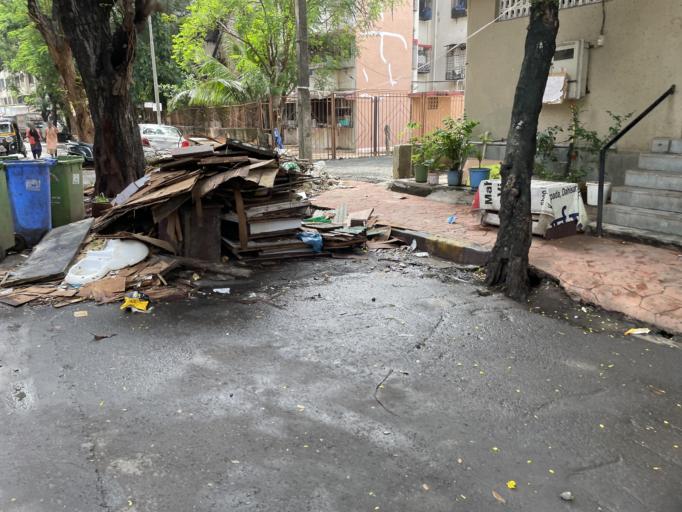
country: IN
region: Maharashtra
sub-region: Mumbai Suburban
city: Borivli
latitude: 19.2568
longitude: 72.8547
